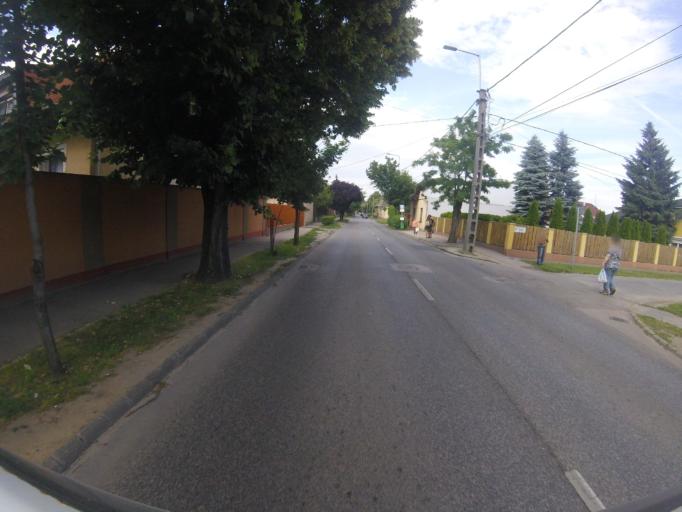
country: HU
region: Budapest
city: Budapest XXI. keruelet
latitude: 47.4139
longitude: 19.0694
